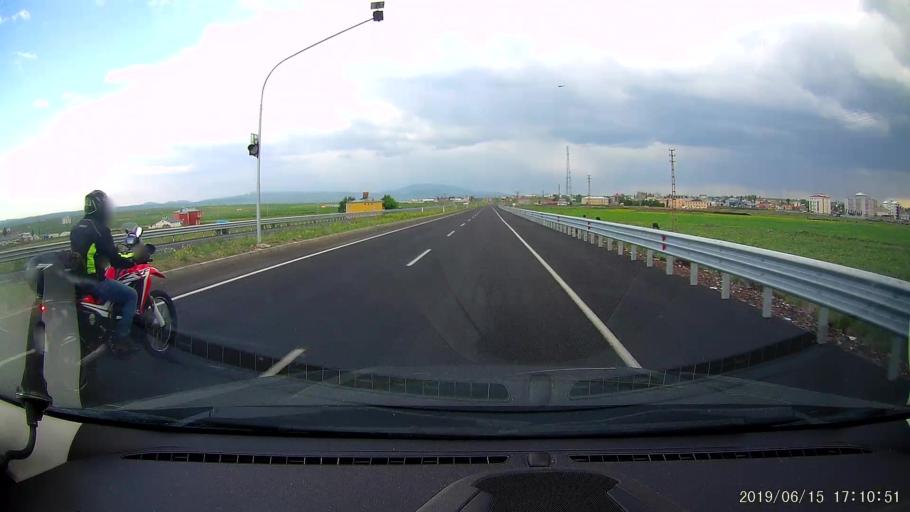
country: TR
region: Kars
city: Kars
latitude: 40.6177
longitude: 43.1334
